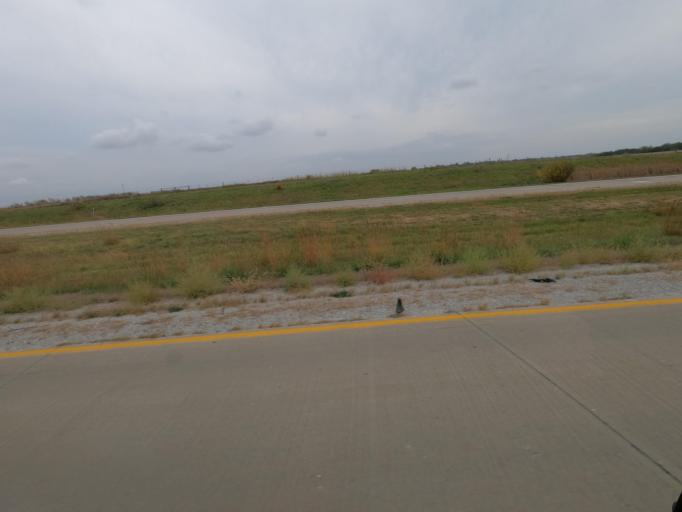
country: US
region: Iowa
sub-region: Jasper County
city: Monroe
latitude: 41.5288
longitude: -93.1304
